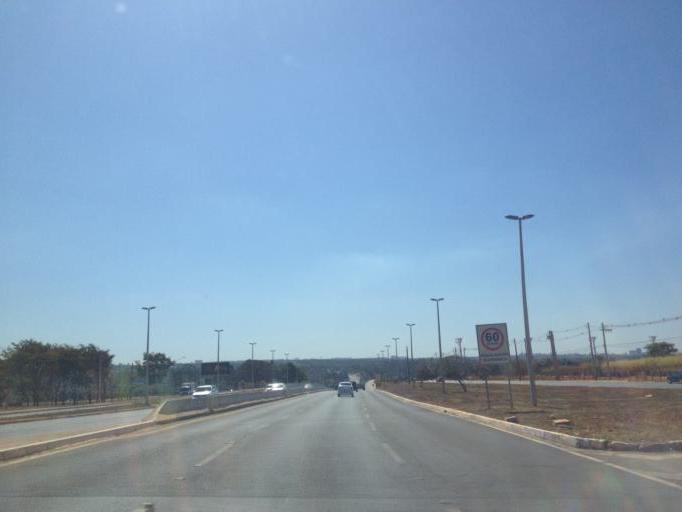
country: BR
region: Federal District
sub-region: Brasilia
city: Brasilia
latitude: -15.8661
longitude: -47.9364
